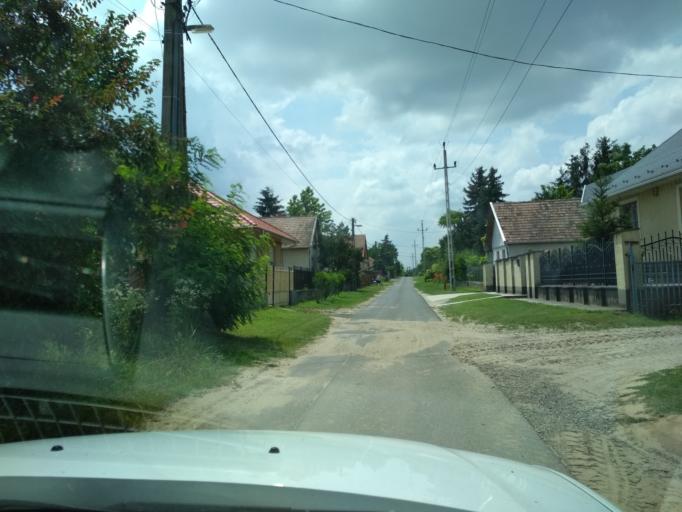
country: HU
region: Pest
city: Tapiobicske
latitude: 47.3594
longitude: 19.6854
